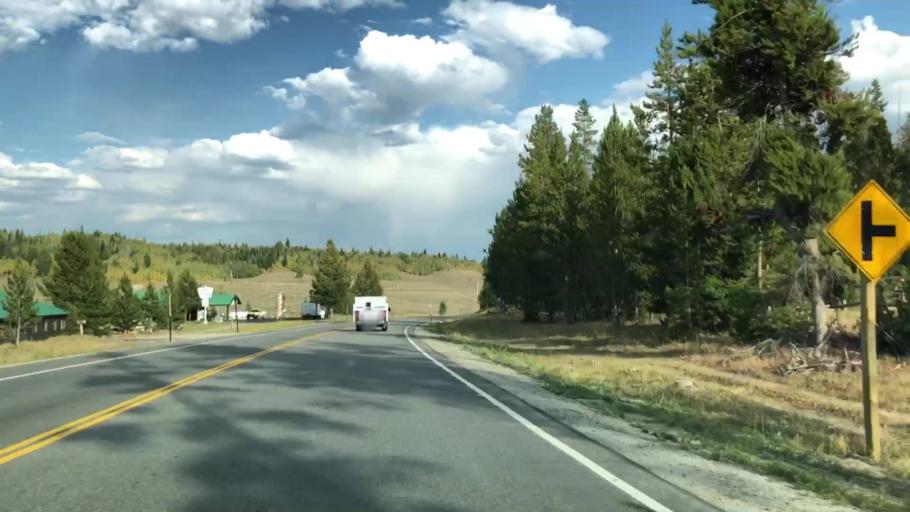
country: US
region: Wyoming
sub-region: Sublette County
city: Pinedale
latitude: 43.1326
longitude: -110.1980
